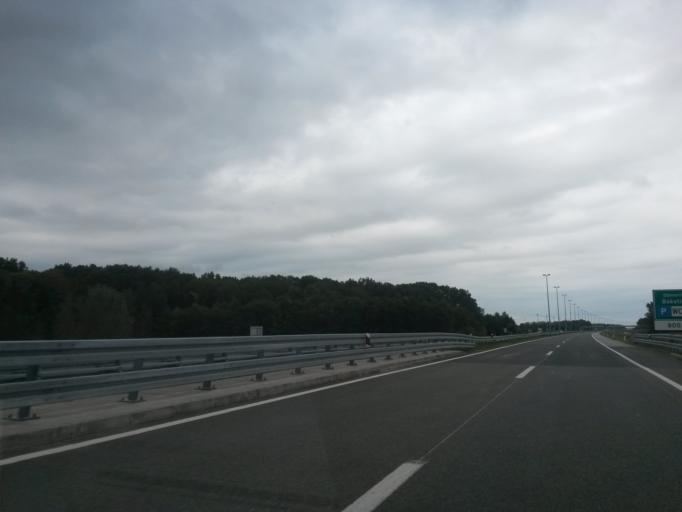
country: HR
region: Osjecko-Baranjska
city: Vuka
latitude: 45.4653
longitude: 18.4752
